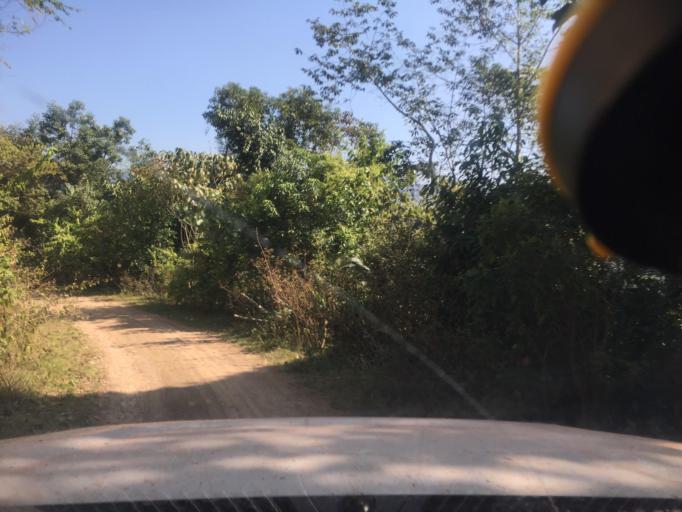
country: LA
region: Phongsali
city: Phongsali
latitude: 21.7025
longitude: 102.3904
